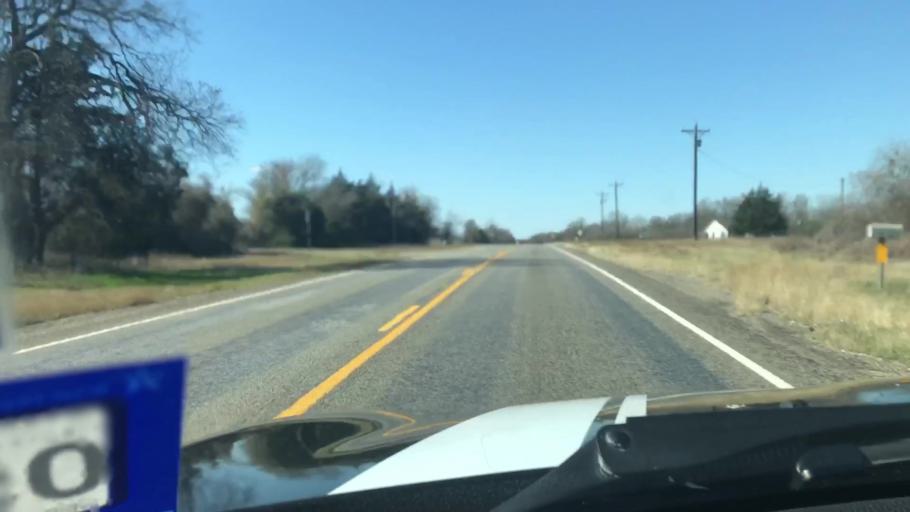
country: US
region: Texas
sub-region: Robertson County
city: Calvert
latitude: 30.8851
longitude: -96.7765
